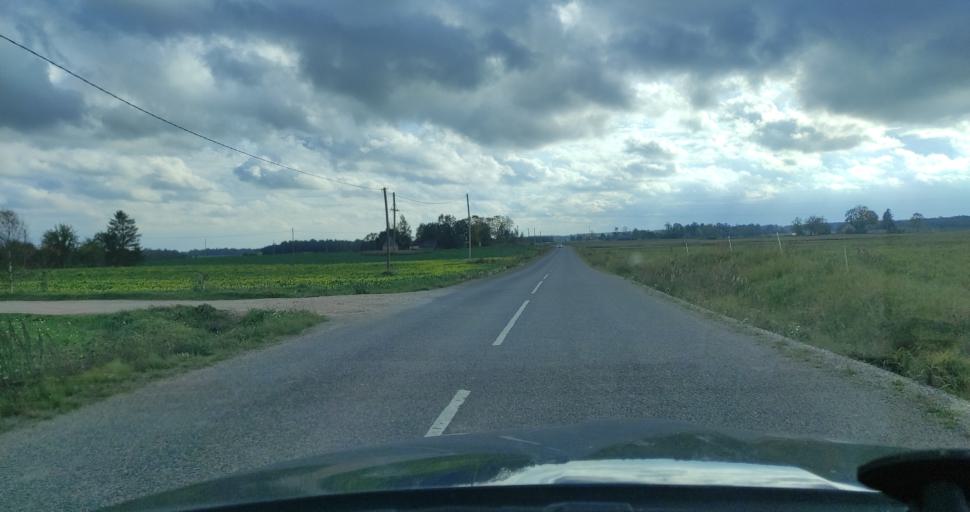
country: LV
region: Talsu Rajons
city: Sabile
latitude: 56.9402
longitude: 22.3965
